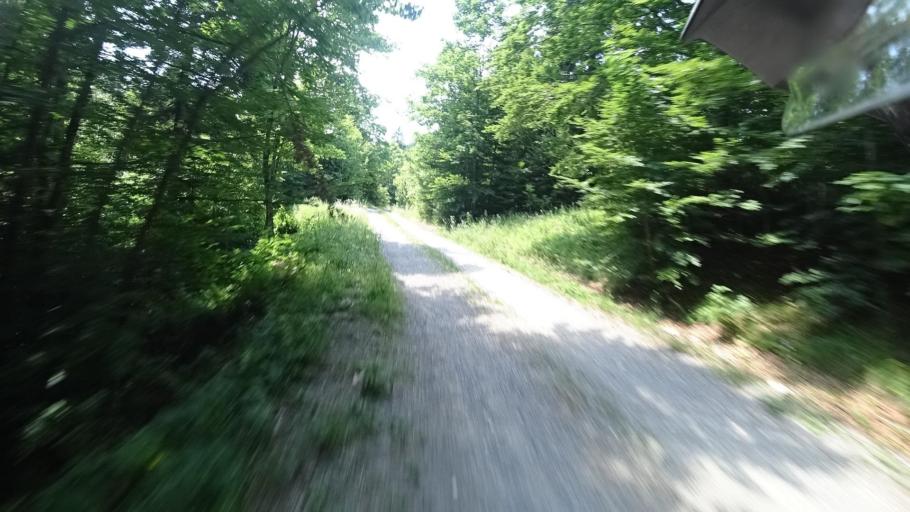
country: HR
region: Primorsko-Goranska
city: Vrbovsko
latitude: 45.3035
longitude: 15.1098
